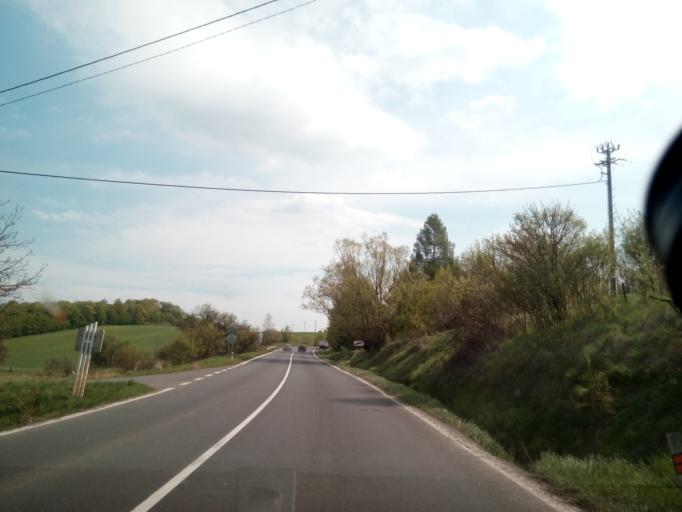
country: SK
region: Presovsky
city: Giraltovce
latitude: 49.0466
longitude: 21.4166
